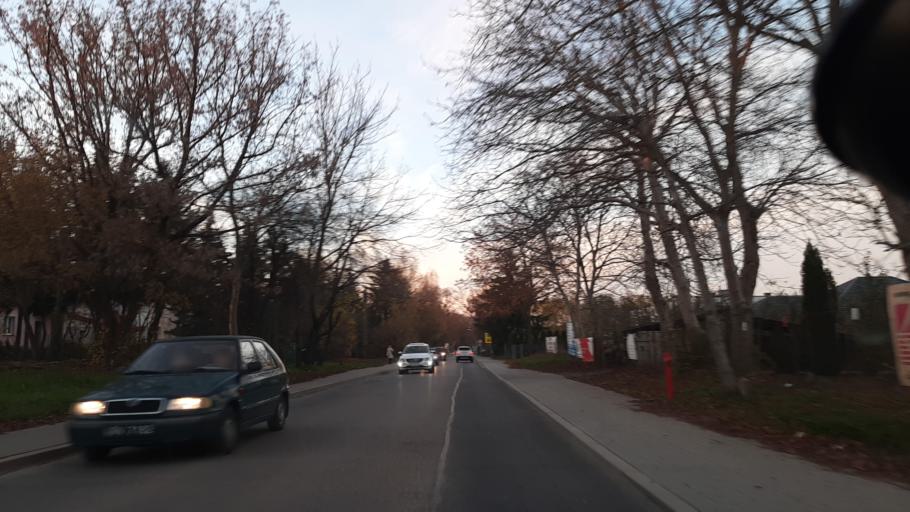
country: PL
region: Lublin Voivodeship
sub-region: Powiat lubelski
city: Lublin
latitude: 51.2741
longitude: 22.5093
